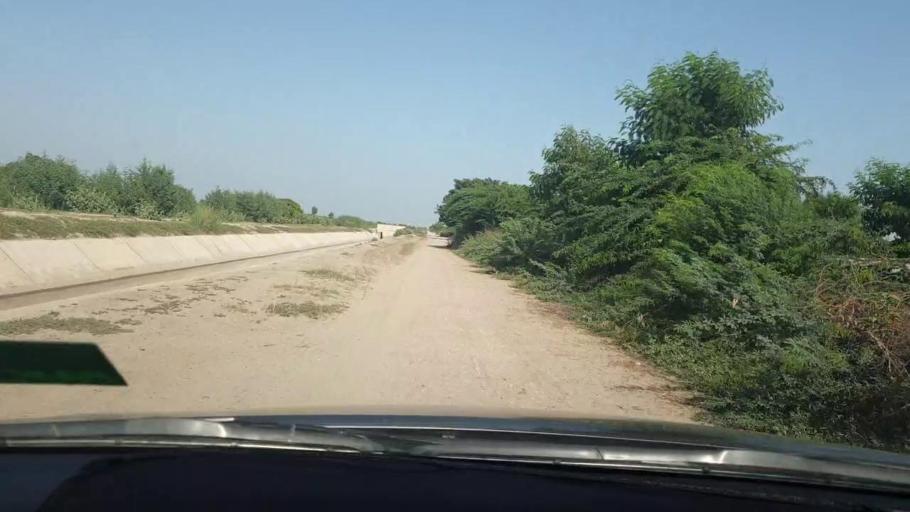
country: PK
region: Sindh
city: Naukot
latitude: 24.9273
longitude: 69.2498
